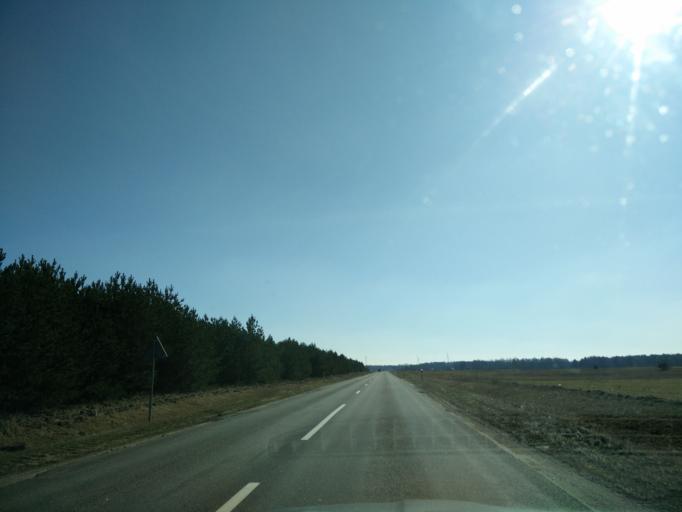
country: LT
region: Klaipedos apskritis
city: Silute
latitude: 55.3247
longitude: 21.5255
